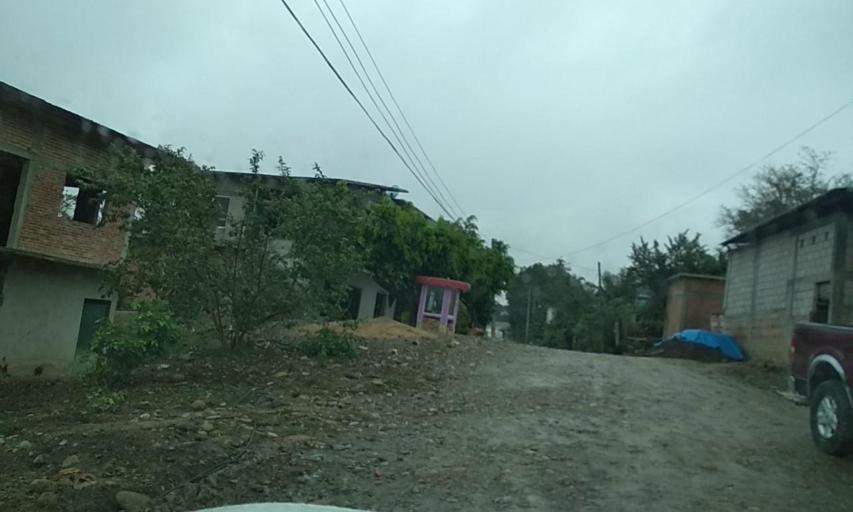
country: MX
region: Veracruz
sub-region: Papantla
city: El Chote
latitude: 20.3594
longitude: -97.3405
